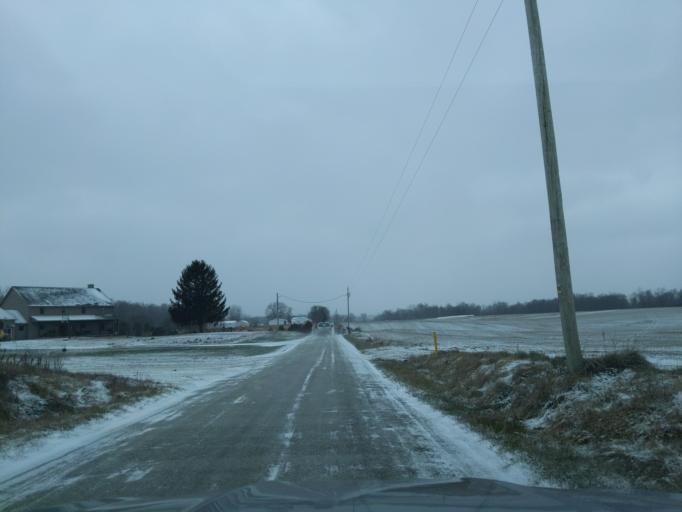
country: US
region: Indiana
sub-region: Decatur County
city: Westport
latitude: 39.2287
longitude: -85.5032
